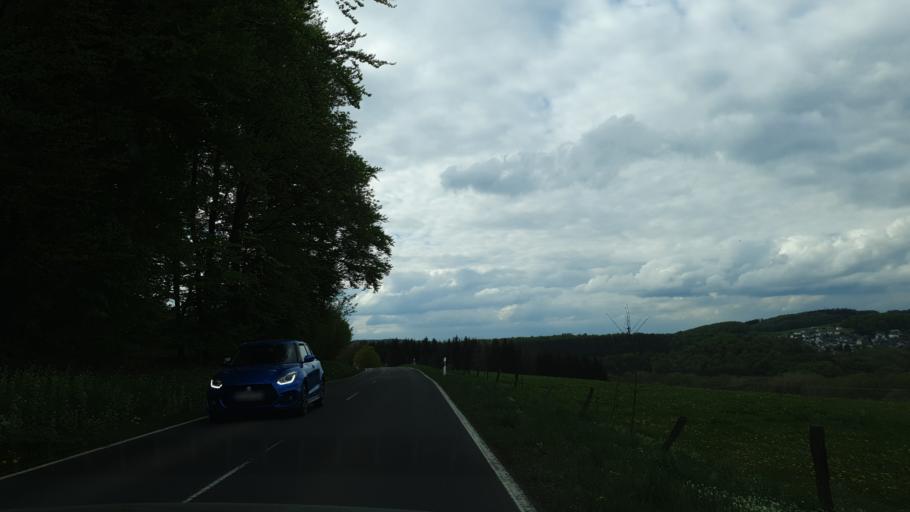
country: DE
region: Rheinland-Pfalz
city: Dreisbach
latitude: 50.6191
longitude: 7.9266
